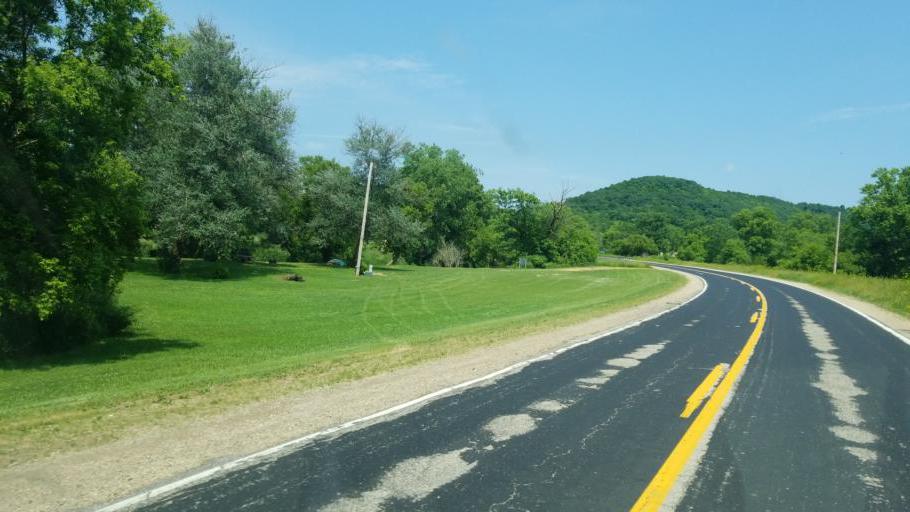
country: US
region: Wisconsin
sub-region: Monroe County
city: Cashton
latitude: 43.5562
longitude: -90.6514
